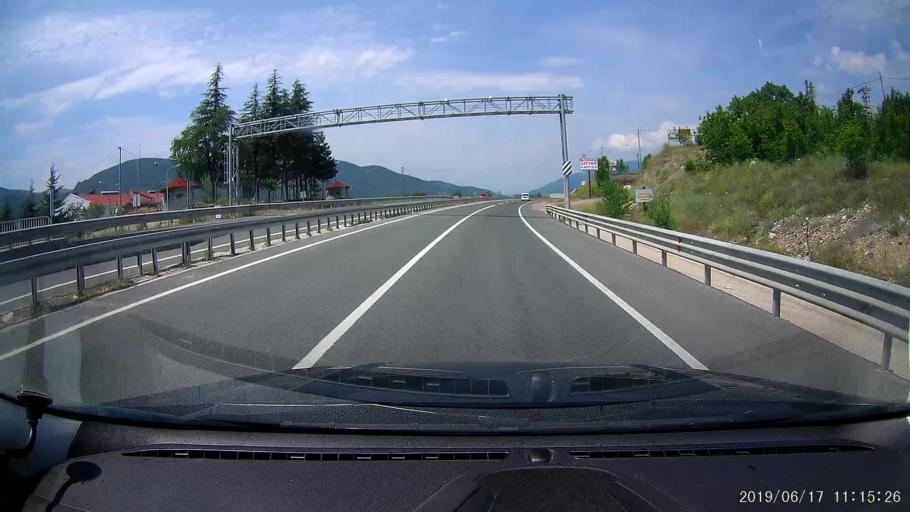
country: TR
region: Kastamonu
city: Tosya
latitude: 40.9515
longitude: 33.9237
